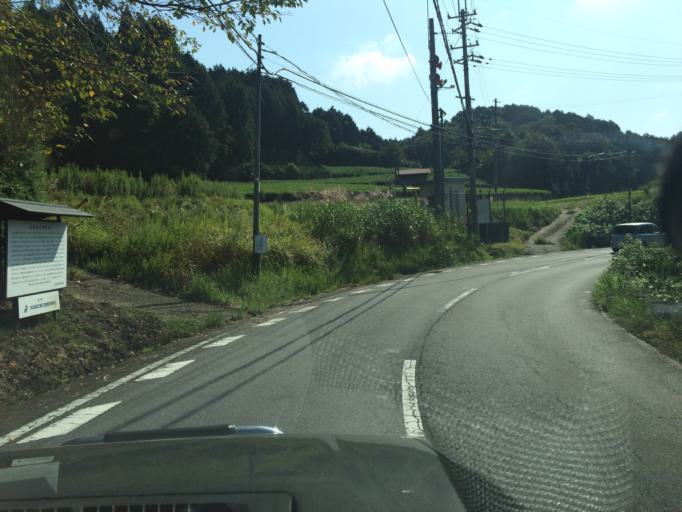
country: JP
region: Mie
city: Ueno-ebisumachi
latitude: 34.7362
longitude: 135.9751
